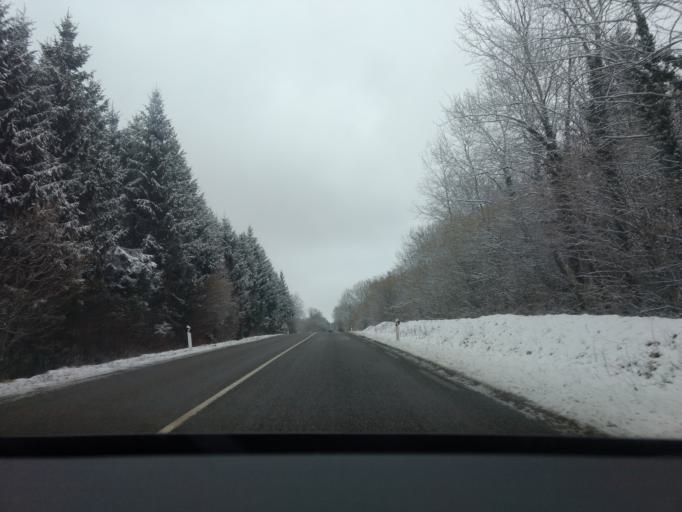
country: FR
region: Franche-Comte
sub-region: Departement du Jura
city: Champagnole
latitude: 46.7837
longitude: 5.8590
